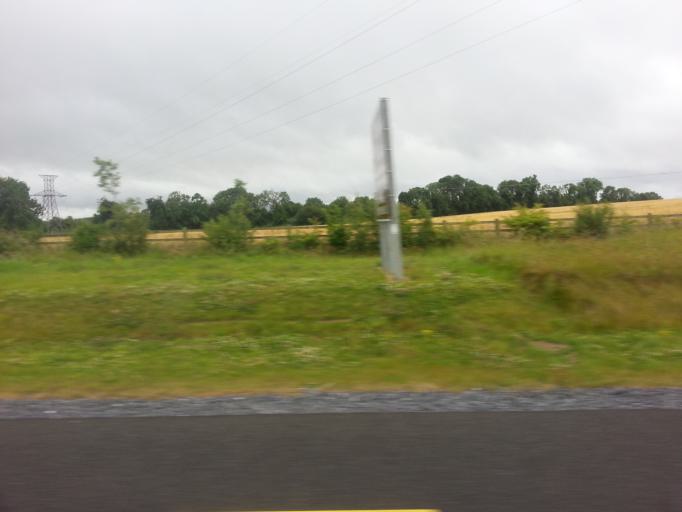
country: IE
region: Leinster
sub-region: Kilkenny
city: Kilkenny
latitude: 52.6436
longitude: -7.1775
